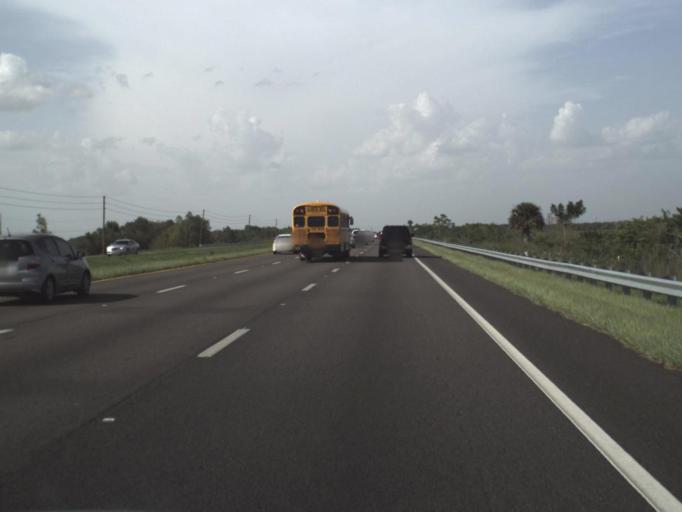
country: US
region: Florida
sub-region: Polk County
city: Dundee
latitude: 27.9839
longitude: -81.6309
